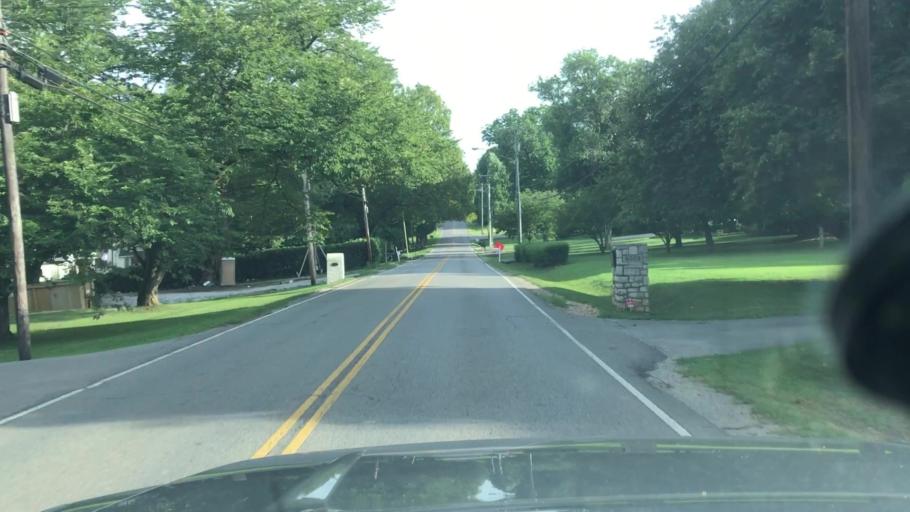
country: US
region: Tennessee
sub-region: Davidson County
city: Belle Meade
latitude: 36.1064
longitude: -86.8379
